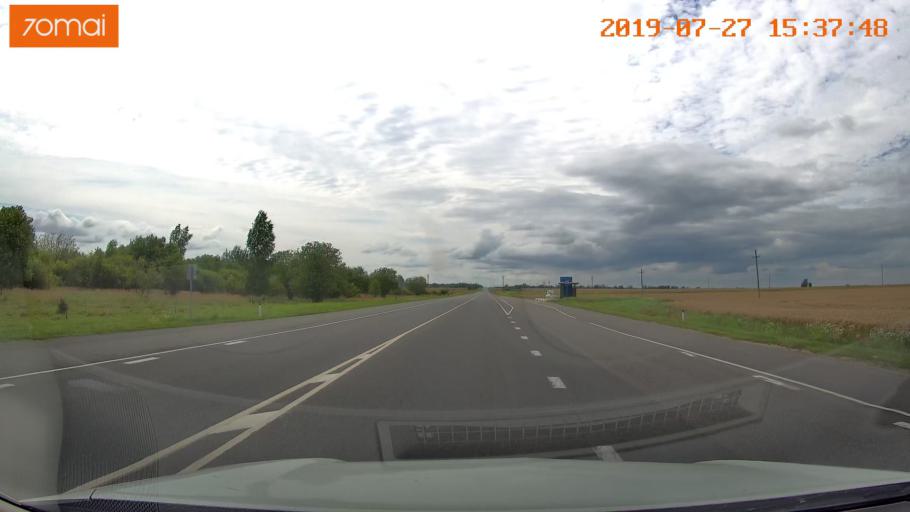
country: RU
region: Kaliningrad
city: Gusev
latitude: 54.6094
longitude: 22.3314
